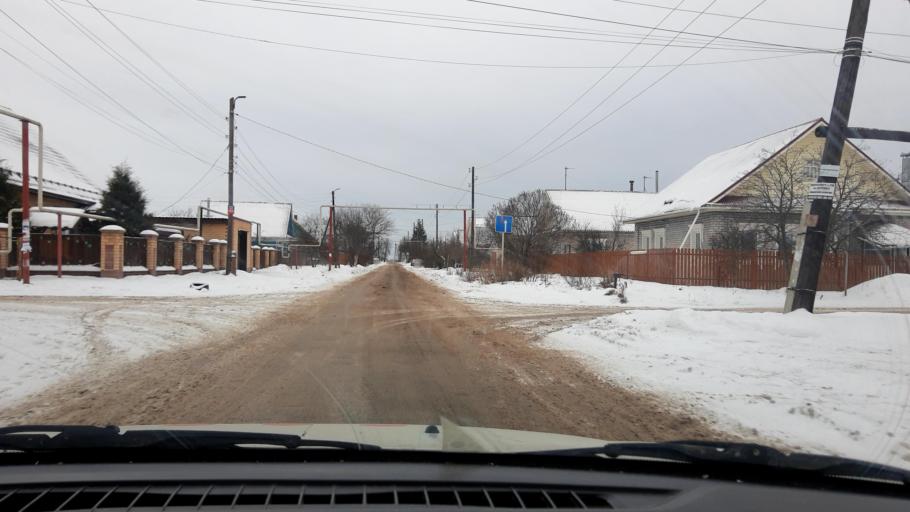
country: RU
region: Nizjnij Novgorod
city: Gorodets
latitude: 56.6641
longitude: 43.4788
